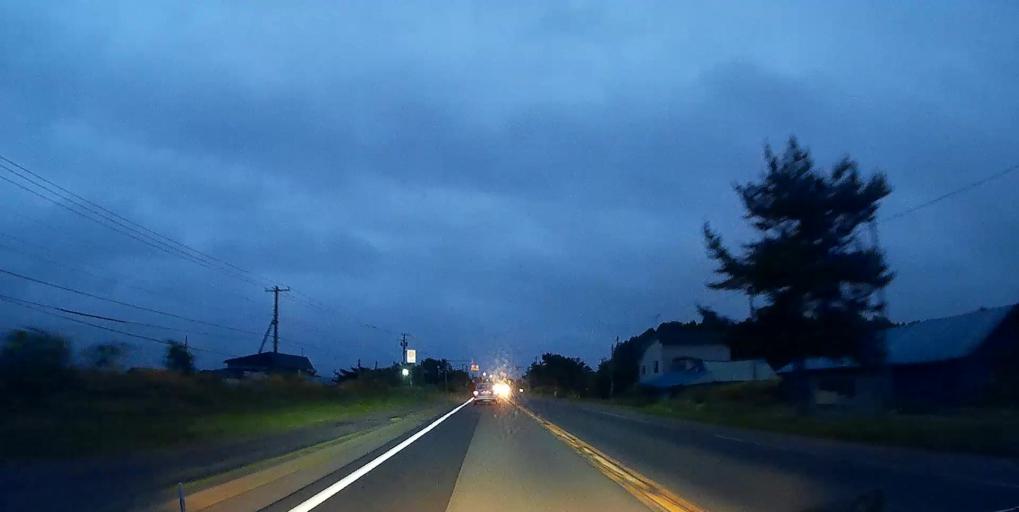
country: JP
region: Hokkaido
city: Nanae
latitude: 42.2227
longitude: 140.3658
